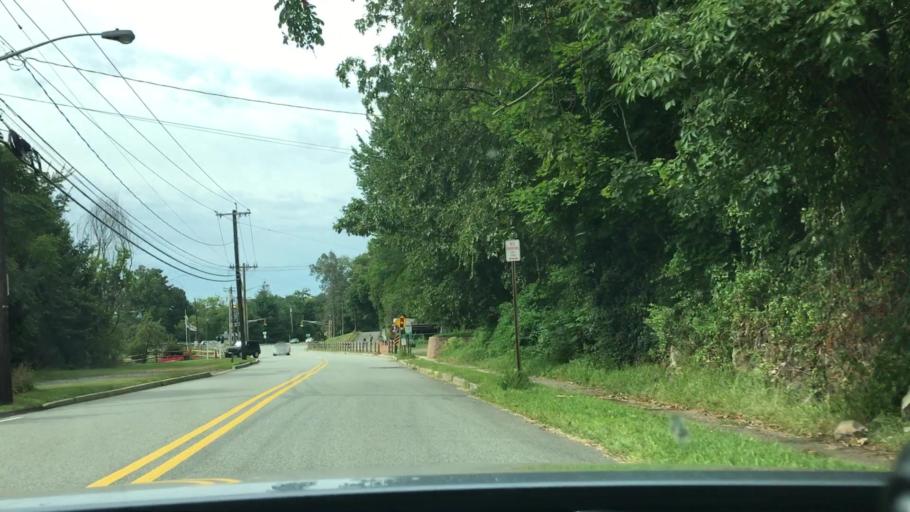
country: US
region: New Jersey
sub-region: Bergen County
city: Woodcliff Lake
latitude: 41.0093
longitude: -74.0706
